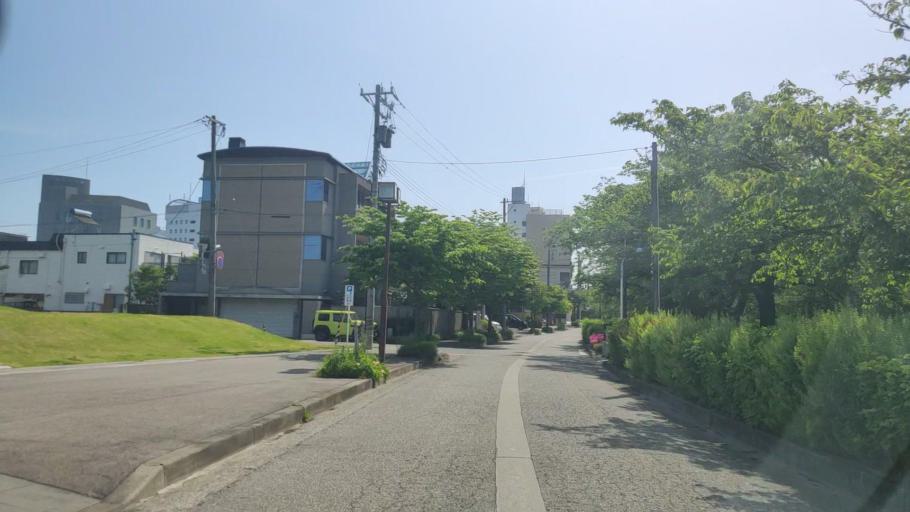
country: JP
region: Toyama
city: Toyama-shi
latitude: 36.6945
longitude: 137.2061
